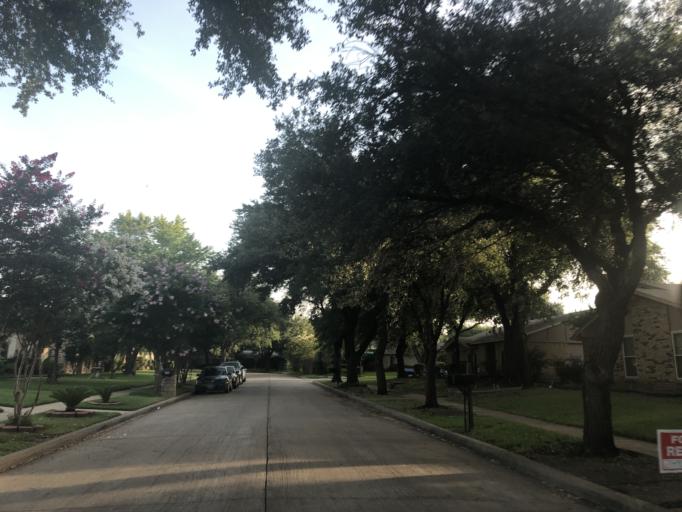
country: US
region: Texas
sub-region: Dallas County
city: Sunnyvale
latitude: 32.8378
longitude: -96.5895
